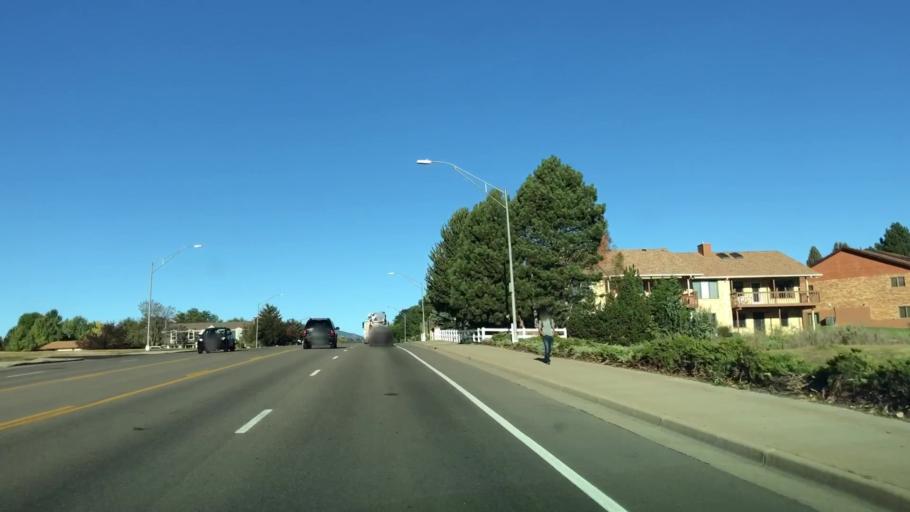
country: US
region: Colorado
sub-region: Larimer County
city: Loveland
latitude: 40.4218
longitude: -105.1097
